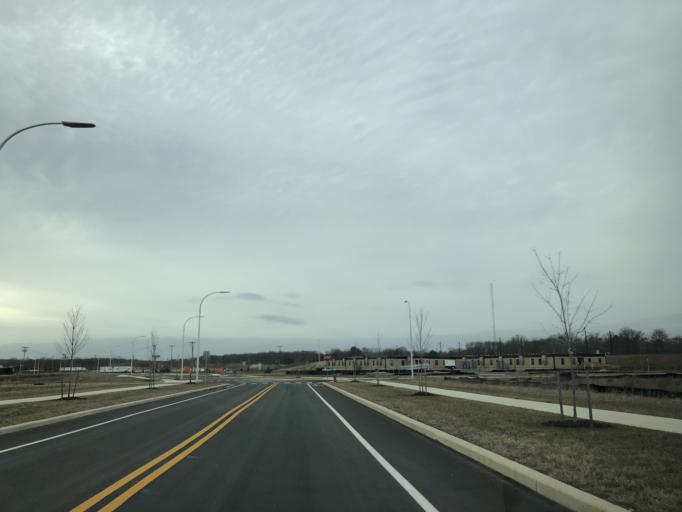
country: US
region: Delaware
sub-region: New Castle County
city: Newark
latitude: 39.6669
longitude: -75.7549
